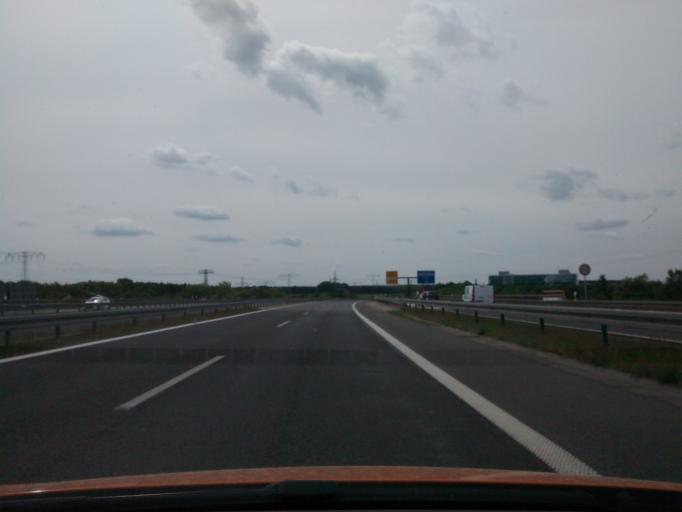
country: DE
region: Brandenburg
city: Ludwigsfelde
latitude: 52.3089
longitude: 13.2879
